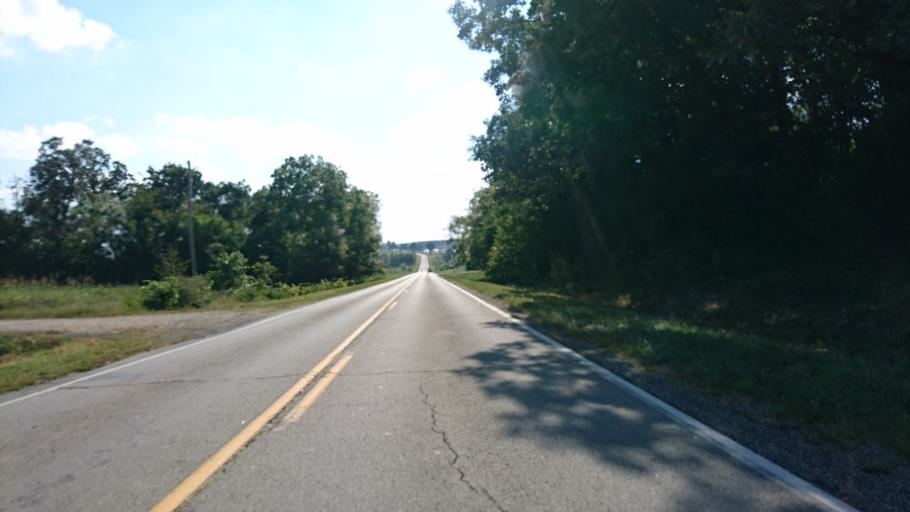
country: US
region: Missouri
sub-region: Laclede County
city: Lebanon
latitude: 37.6379
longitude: -92.6787
